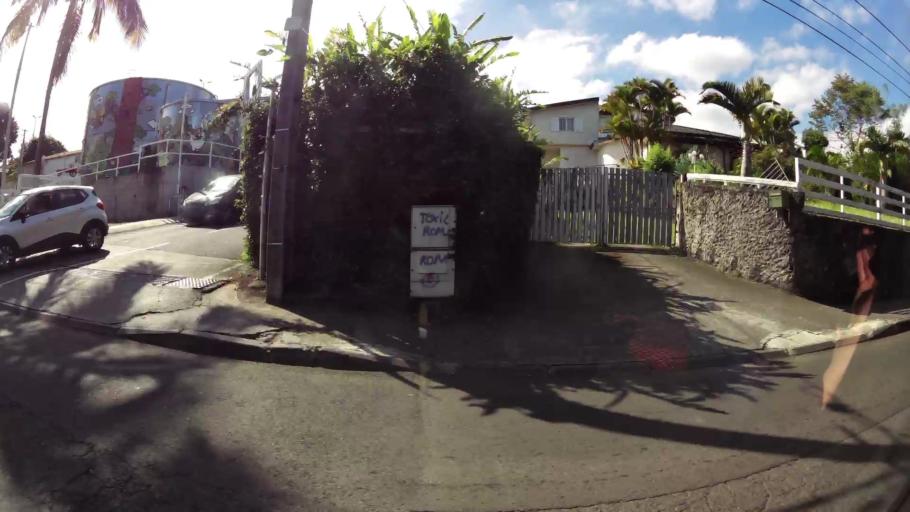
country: RE
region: Reunion
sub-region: Reunion
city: Le Tampon
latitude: -21.2833
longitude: 55.5169
